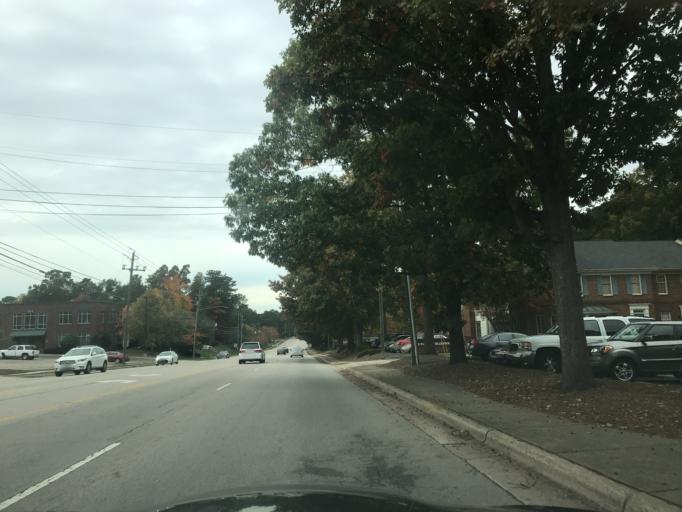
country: US
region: North Carolina
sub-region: Wake County
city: West Raleigh
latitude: 35.8563
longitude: -78.6421
